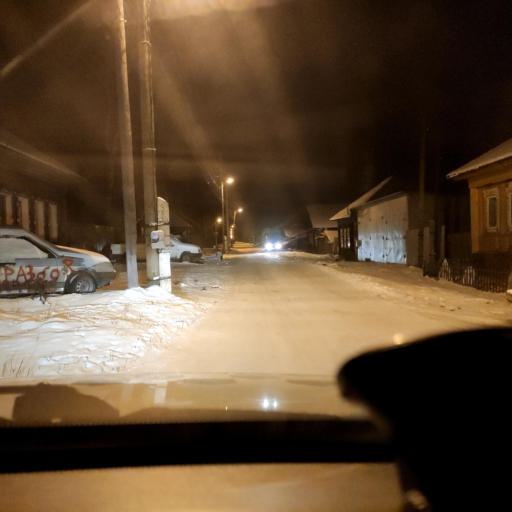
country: RU
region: Perm
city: Perm
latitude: 58.0270
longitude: 56.3226
